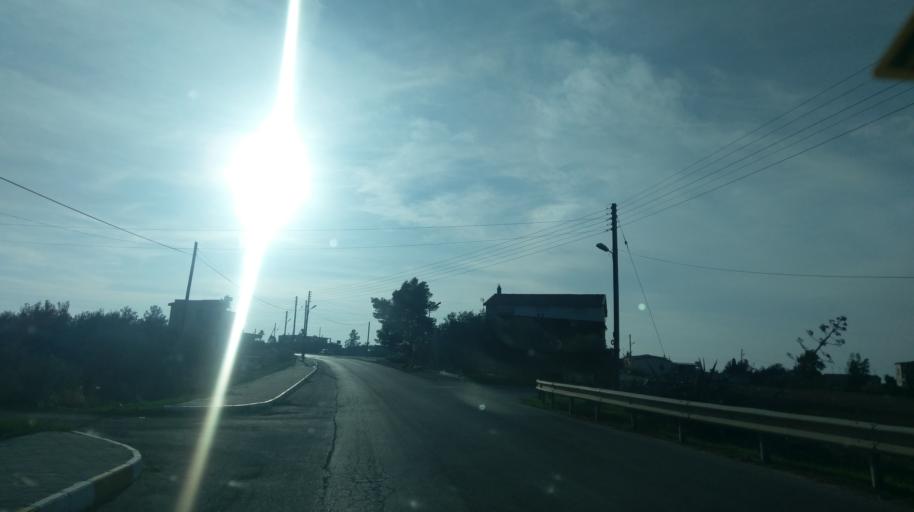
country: CY
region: Larnaka
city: Pergamos
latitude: 35.1072
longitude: 33.7199
